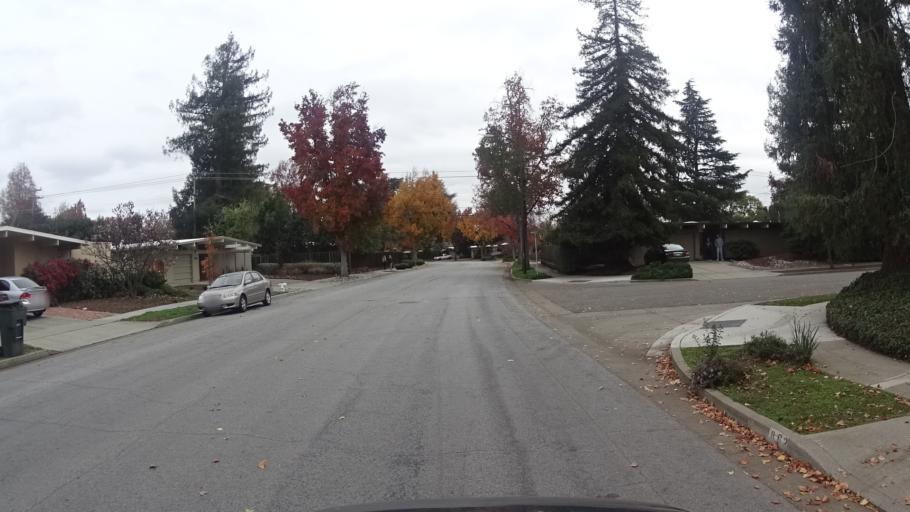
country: US
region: California
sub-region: Santa Clara County
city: Sunnyvale
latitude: 37.3555
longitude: -122.0486
